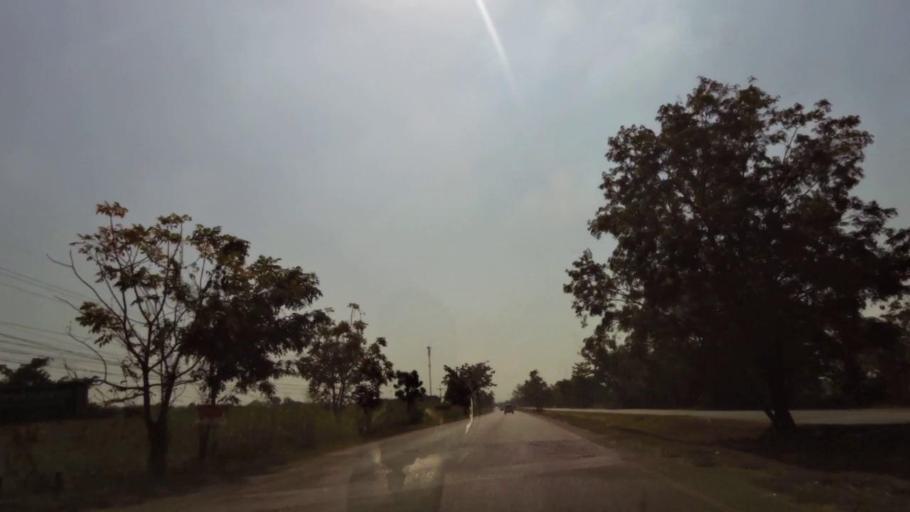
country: TH
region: Phichit
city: Wachira Barami
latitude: 16.3620
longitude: 100.1303
